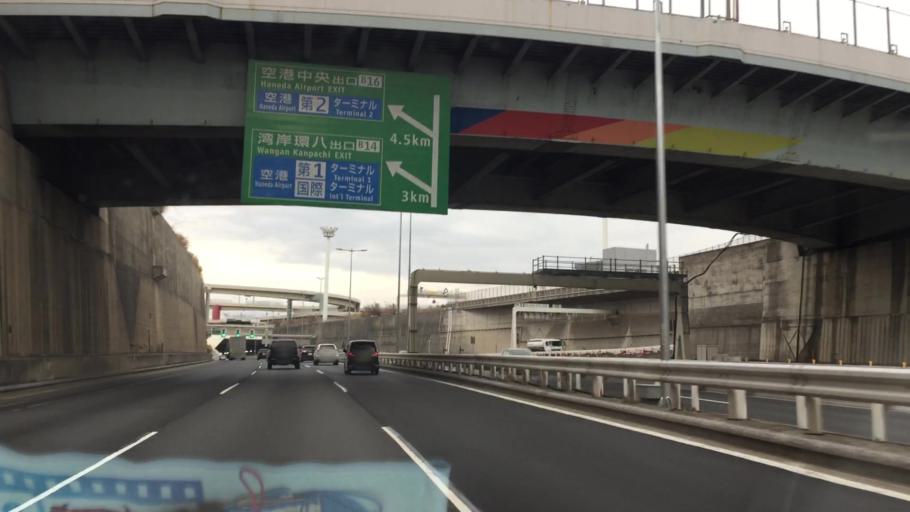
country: JP
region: Kanagawa
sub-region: Kawasaki-shi
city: Kawasaki
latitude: 35.5142
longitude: 139.7883
